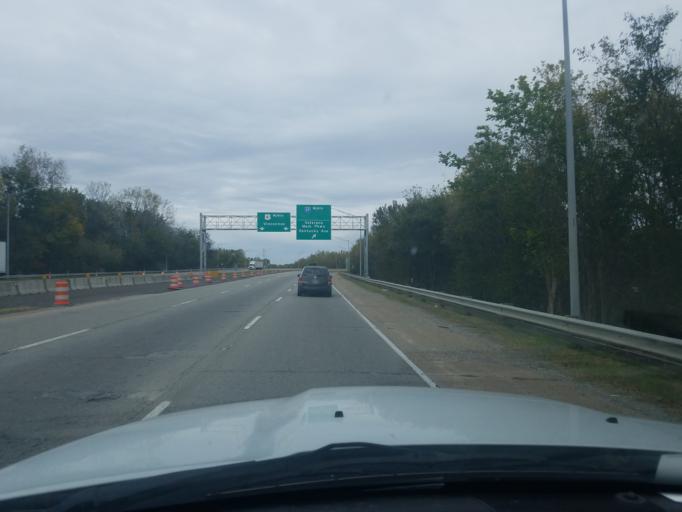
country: US
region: Indiana
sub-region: Vanderburgh County
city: Evansville
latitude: 37.9309
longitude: -87.5481
